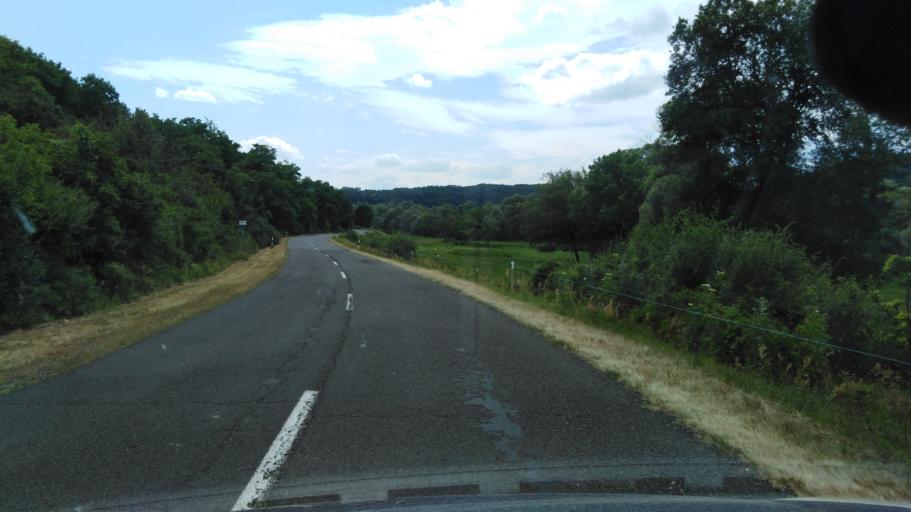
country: HU
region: Nograd
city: Szecseny
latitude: 48.2043
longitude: 19.5305
